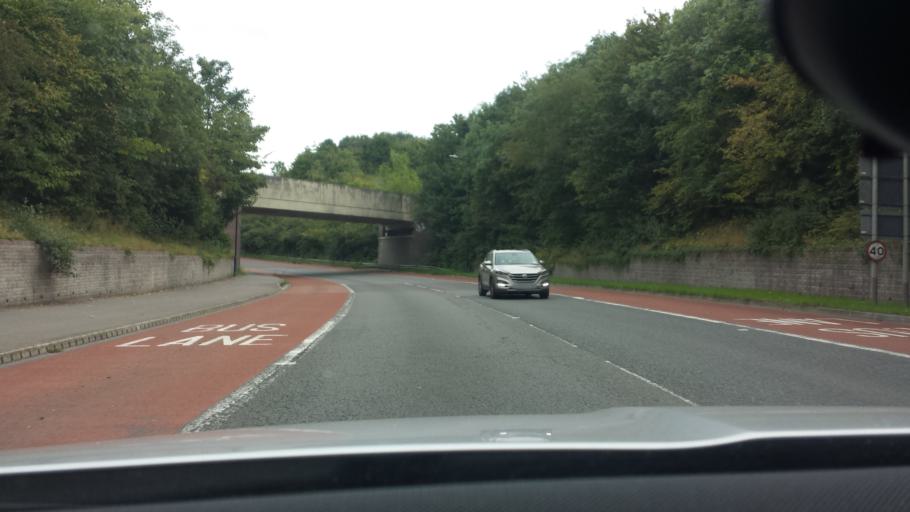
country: GB
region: England
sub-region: Kent
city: Gravesend
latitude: 51.4368
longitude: 0.3451
